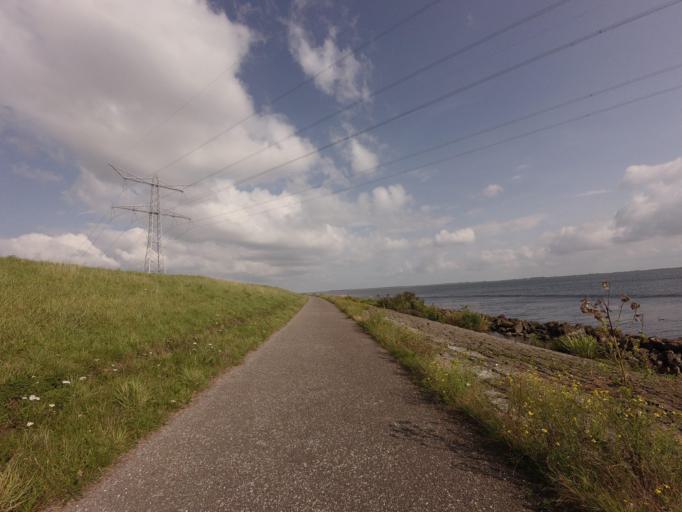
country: NL
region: Flevoland
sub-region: Gemeente Urk
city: Urk
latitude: 52.6132
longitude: 5.6617
